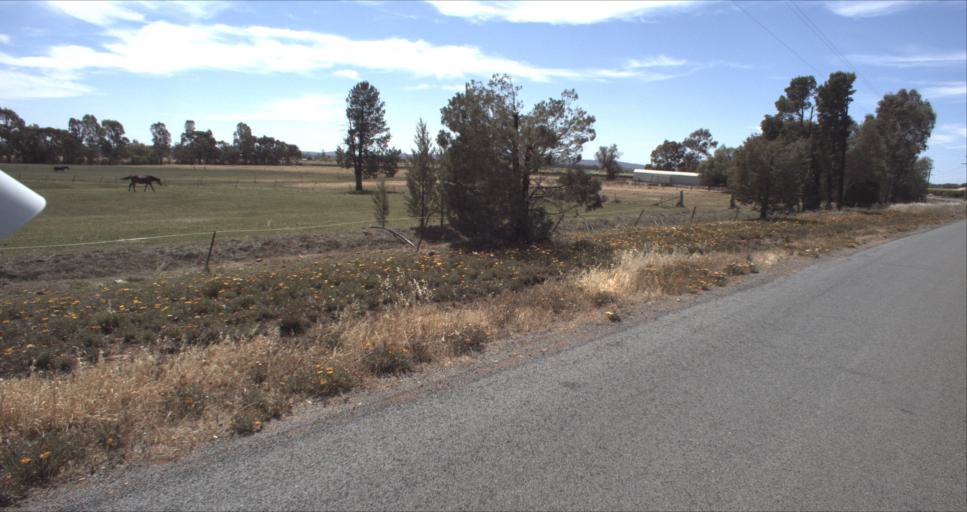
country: AU
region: New South Wales
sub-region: Leeton
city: Leeton
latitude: -34.5719
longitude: 146.4344
